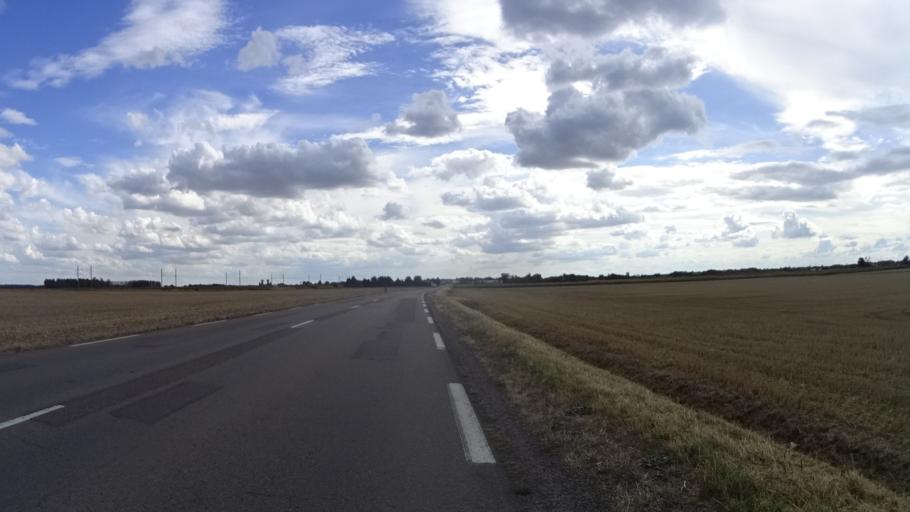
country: FR
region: Bourgogne
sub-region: Departement de la Cote-d'Or
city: Seurre
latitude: 47.0168
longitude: 5.1625
